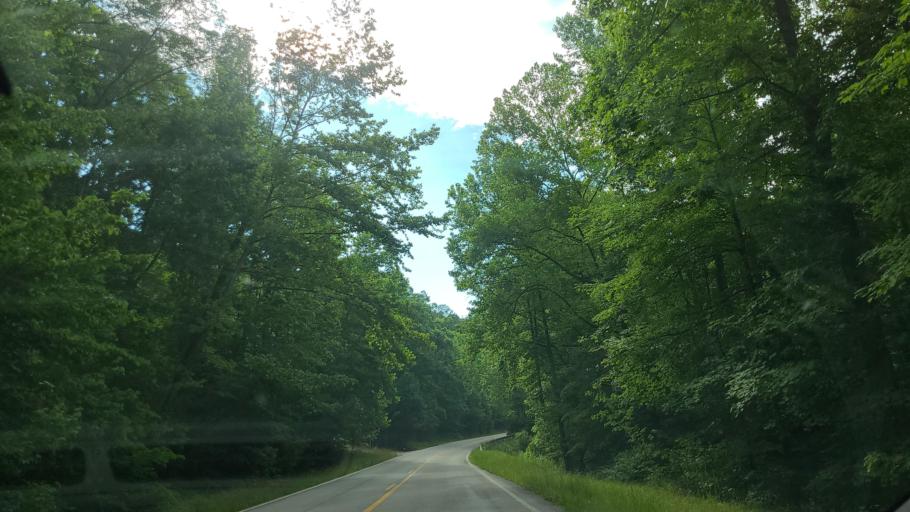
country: US
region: Kentucky
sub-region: Knox County
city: Barbourville
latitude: 36.6809
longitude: -83.9094
